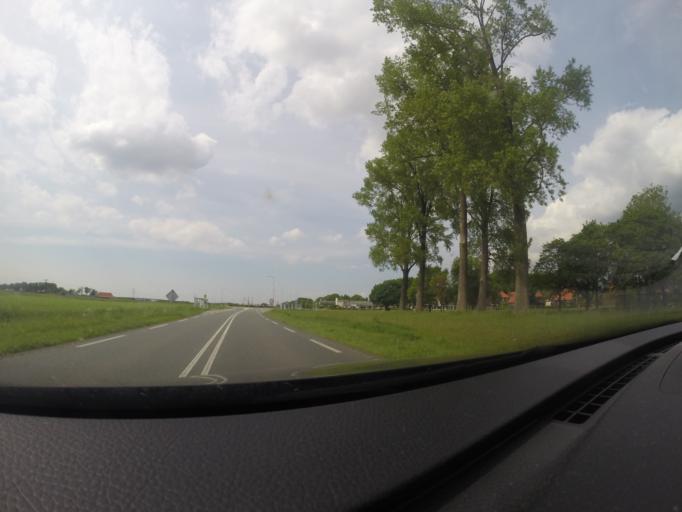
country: NL
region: Flevoland
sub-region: Gemeente Noordoostpolder
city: Ens
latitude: 52.6336
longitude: 5.8245
